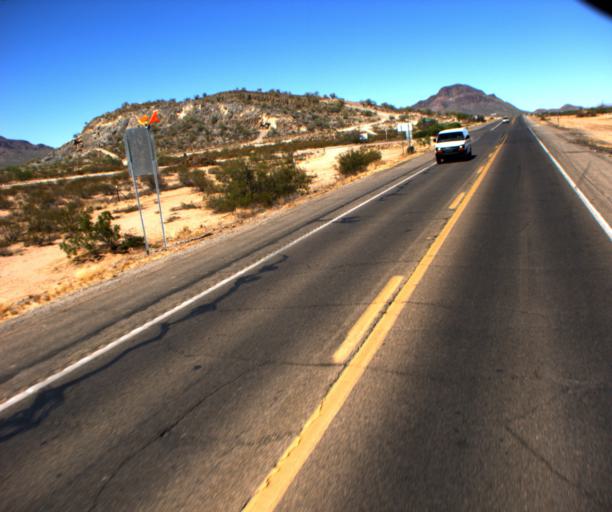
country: US
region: Arizona
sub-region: Pima County
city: Valencia West
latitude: 32.1540
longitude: -111.1167
